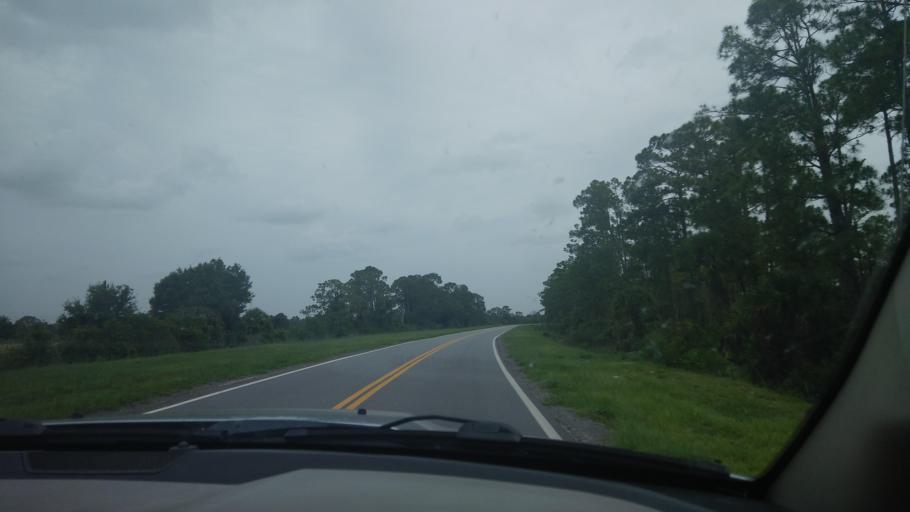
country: US
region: Florida
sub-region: Indian River County
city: Fellsmere
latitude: 27.8374
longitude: -80.6207
